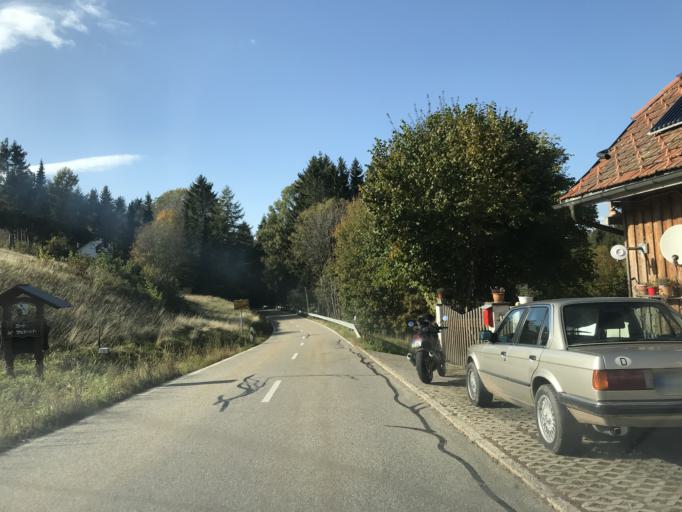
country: DE
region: Baden-Wuerttemberg
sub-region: Freiburg Region
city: Rickenbach
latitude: 47.6378
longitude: 7.9437
